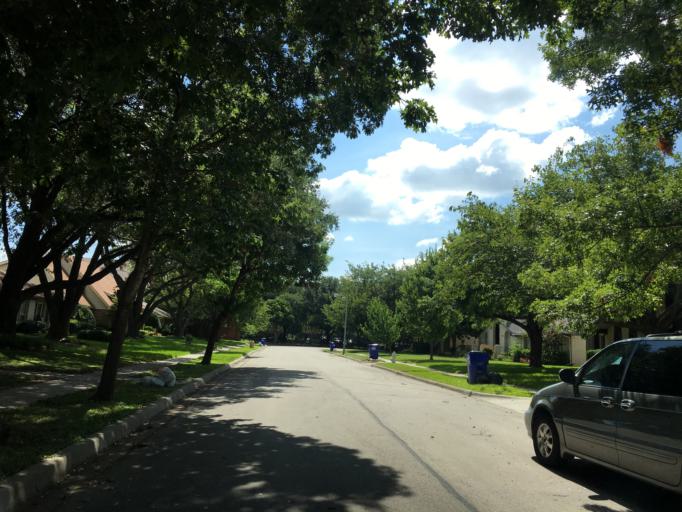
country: US
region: Texas
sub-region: Dallas County
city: Farmers Branch
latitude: 32.9250
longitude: -96.8761
